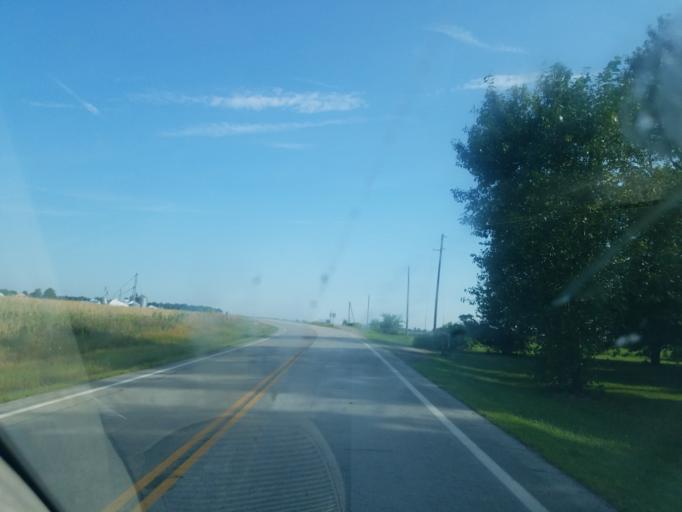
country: US
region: Ohio
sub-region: Hardin County
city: Forest
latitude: 40.7799
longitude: -83.4679
